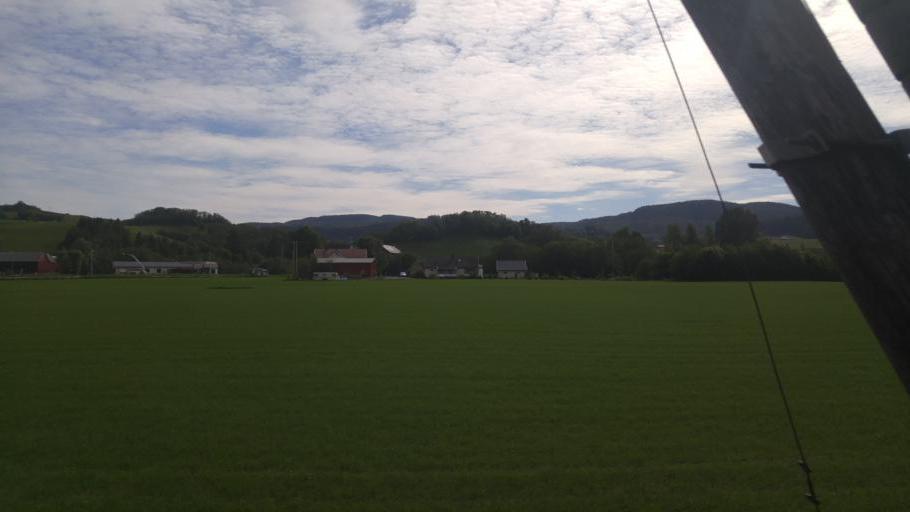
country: NO
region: Sor-Trondelag
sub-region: Melhus
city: Lundamo
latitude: 63.1852
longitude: 10.3086
